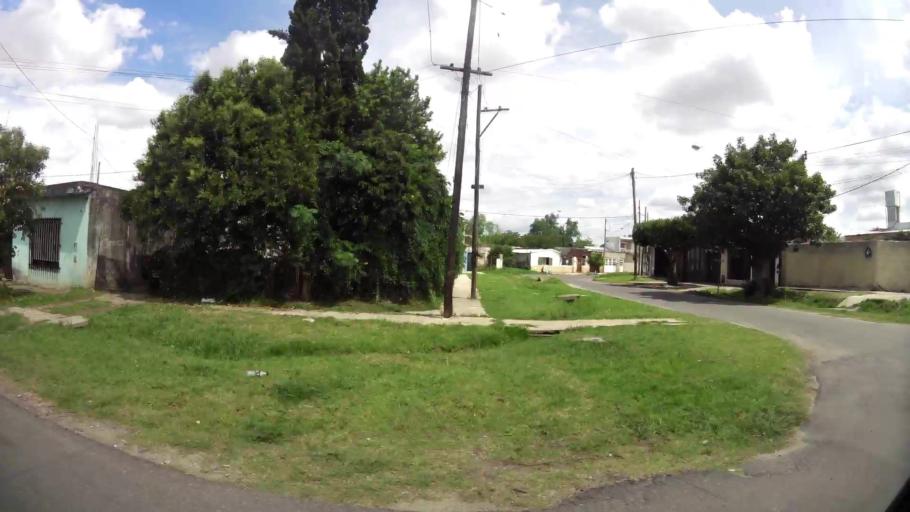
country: AR
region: Santa Fe
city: Gobernador Galvez
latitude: -33.0116
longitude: -60.6376
